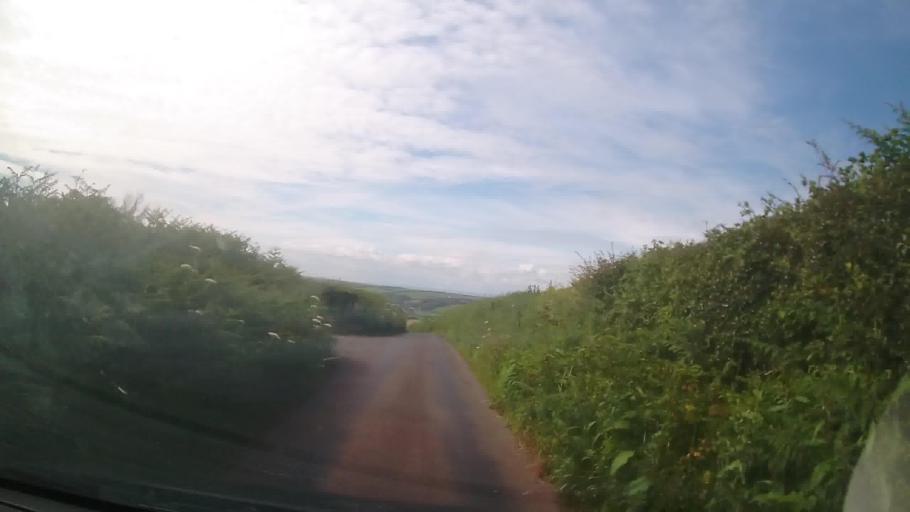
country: GB
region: England
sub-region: Devon
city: Salcombe
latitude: 50.2336
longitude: -3.6718
